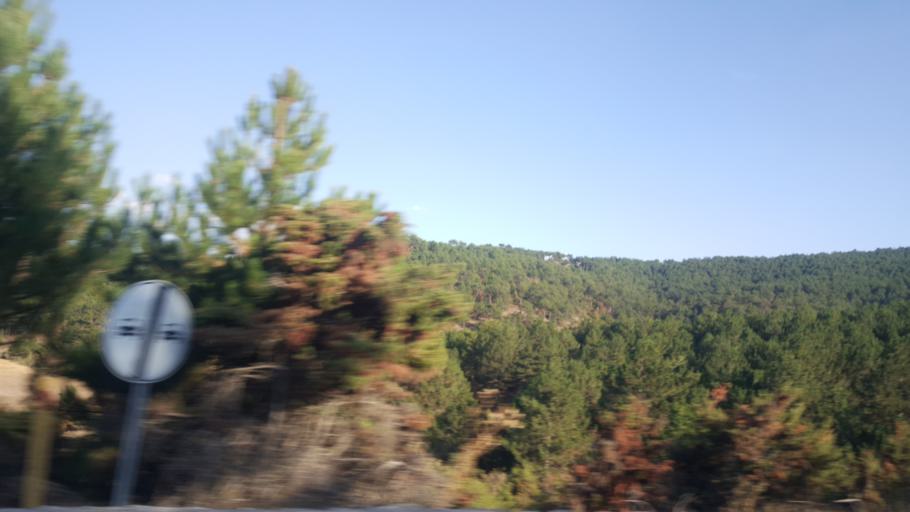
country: TR
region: Eskisehir
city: Kirka
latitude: 39.1190
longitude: 30.5895
